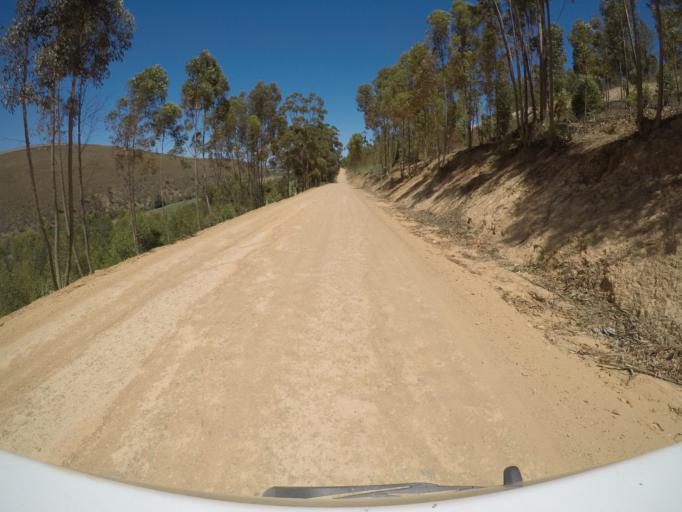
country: ZA
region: Western Cape
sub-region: Overberg District Municipality
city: Grabouw
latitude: -34.2091
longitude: 19.2134
